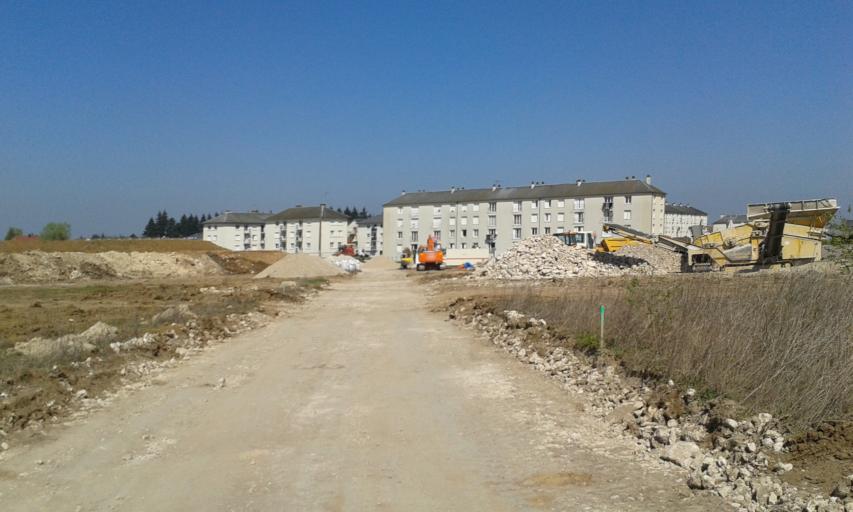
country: FR
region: Centre
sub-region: Departement du Loiret
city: Beaugency
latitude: 47.7780
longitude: 1.6209
